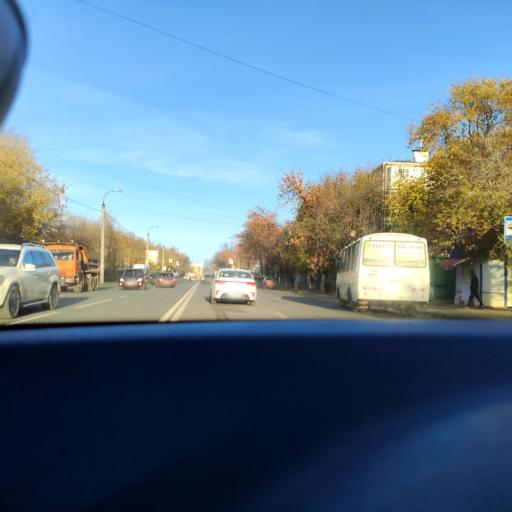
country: RU
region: Samara
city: Samara
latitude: 53.1974
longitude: 50.1578
